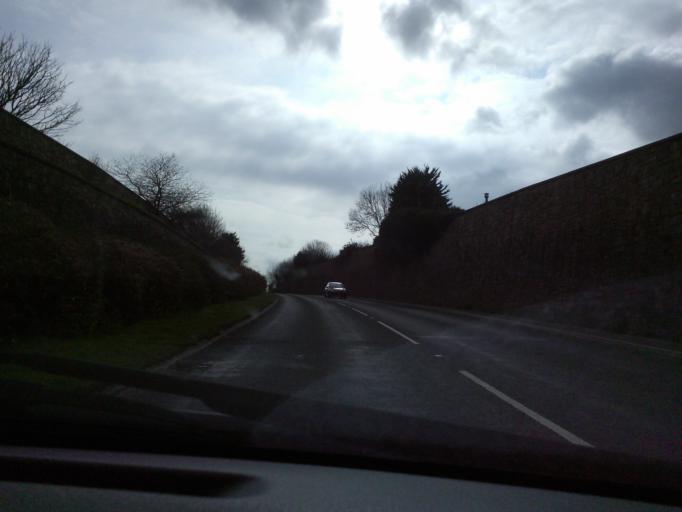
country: GB
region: England
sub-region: Cornwall
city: Penzance
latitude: 50.1283
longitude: -5.5462
